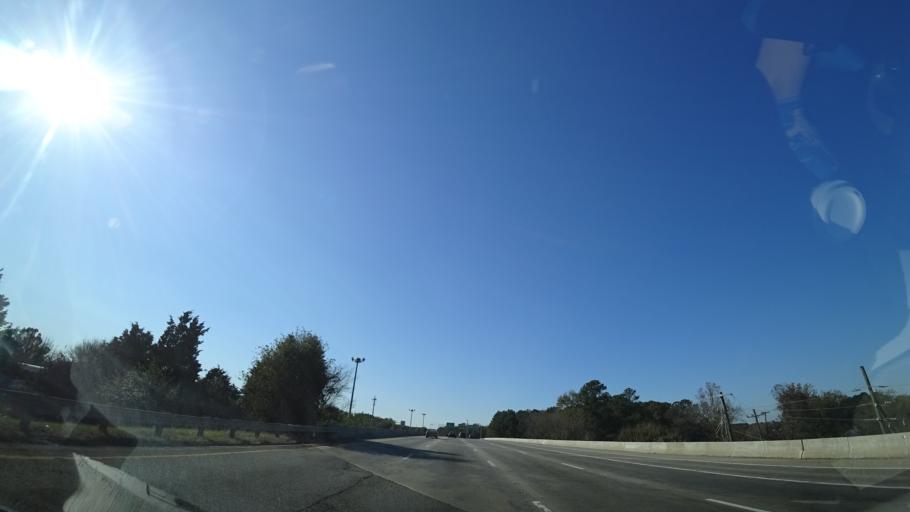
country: US
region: Virginia
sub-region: City of Portsmouth
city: Portsmouth Heights
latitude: 36.7857
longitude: -76.4115
